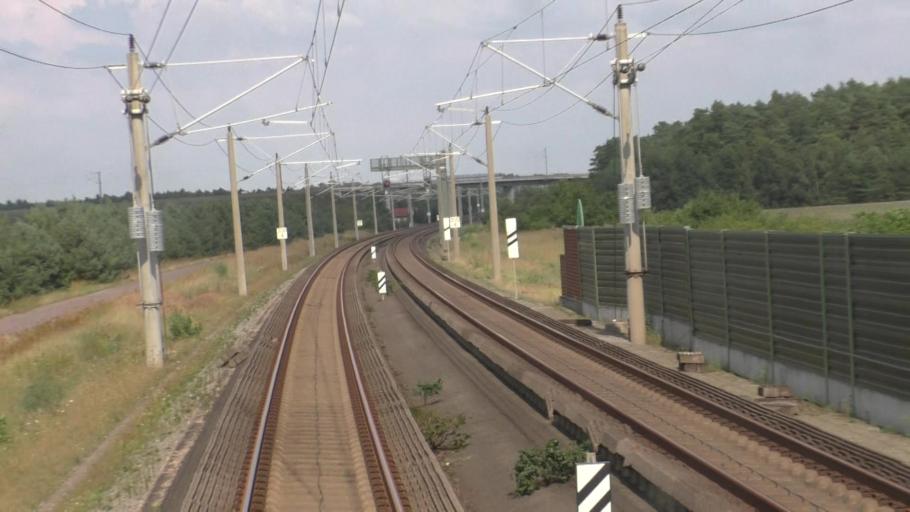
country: DE
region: Saxony-Anhalt
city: Hassel
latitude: 52.5905
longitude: 11.9241
